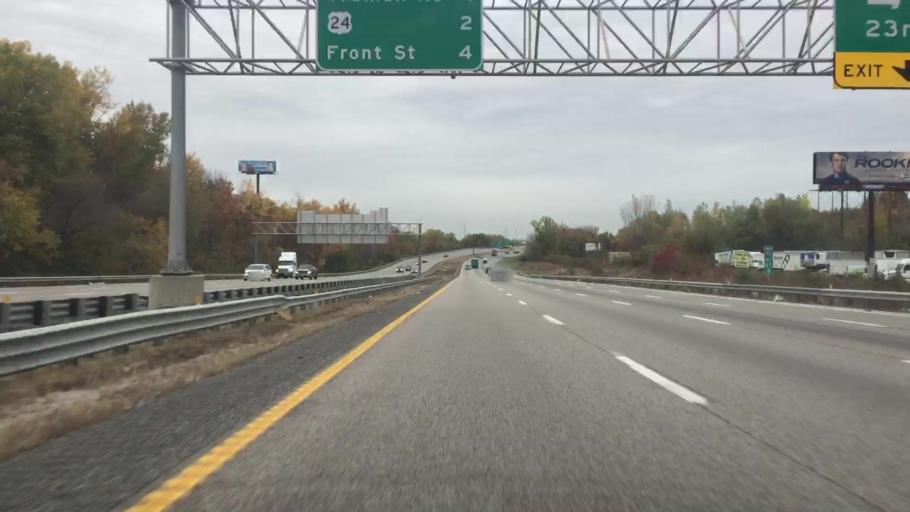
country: US
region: Missouri
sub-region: Jackson County
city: Sugar Creek
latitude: 39.0748
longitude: -94.4891
